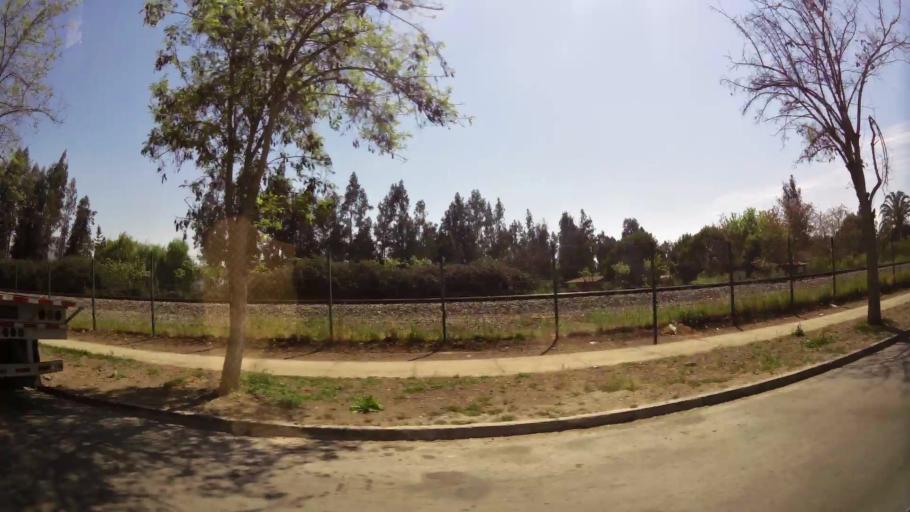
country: CL
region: Santiago Metropolitan
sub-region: Provincia de Talagante
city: Talagante
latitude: -33.6522
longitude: -70.9081
